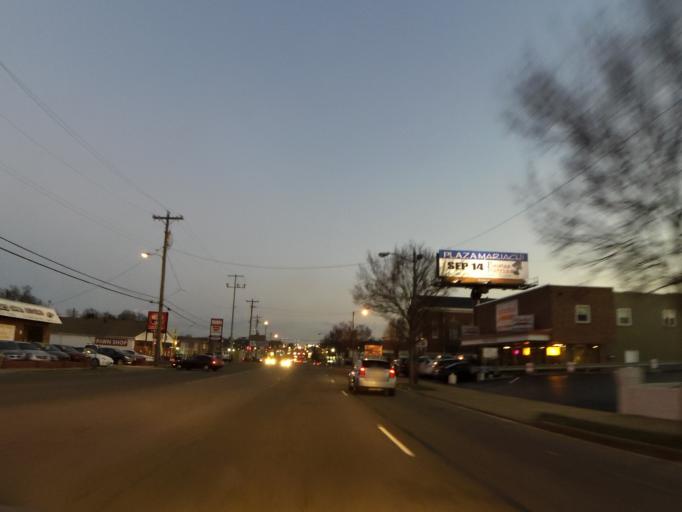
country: US
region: Tennessee
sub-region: Davidson County
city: Oak Hill
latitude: 36.1156
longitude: -86.7477
